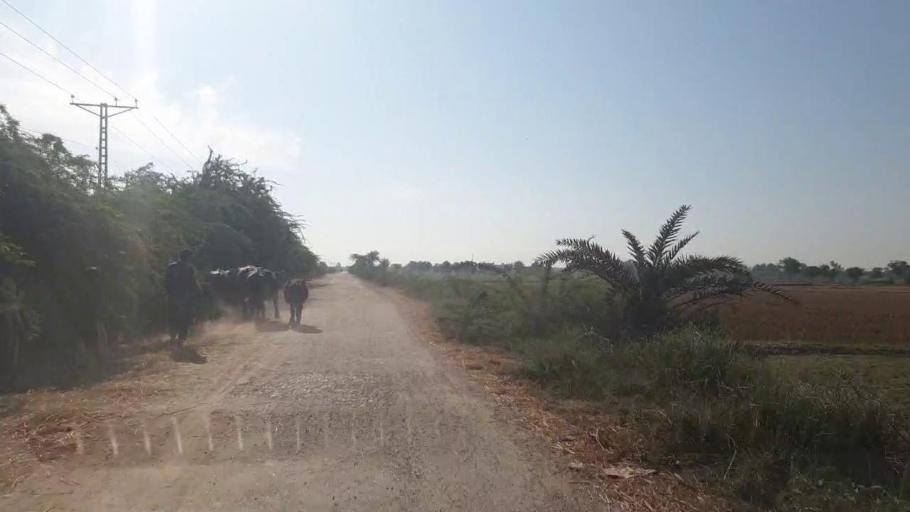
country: PK
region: Sindh
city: Talhar
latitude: 24.9031
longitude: 68.8228
